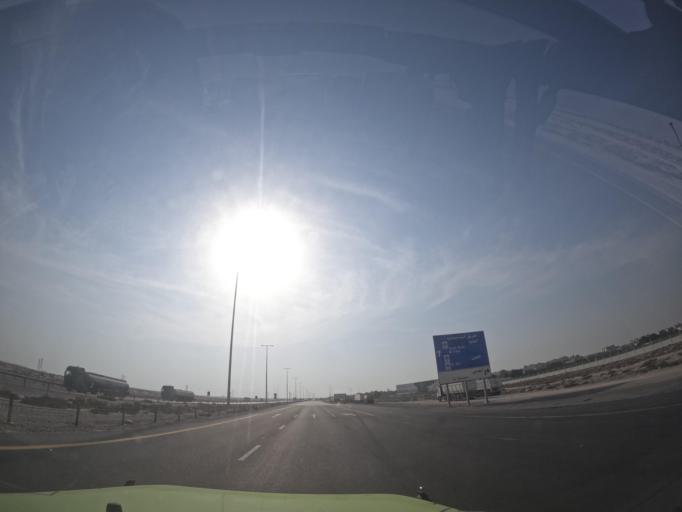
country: AE
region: Dubai
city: Dubai
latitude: 24.8487
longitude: 55.0237
